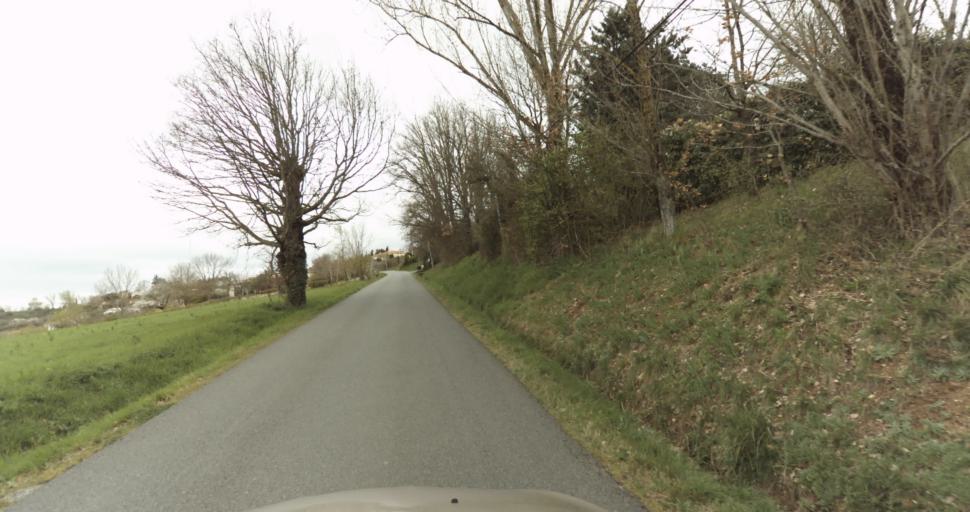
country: FR
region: Midi-Pyrenees
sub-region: Departement du Tarn
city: Puygouzon
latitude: 43.9003
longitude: 2.1614
